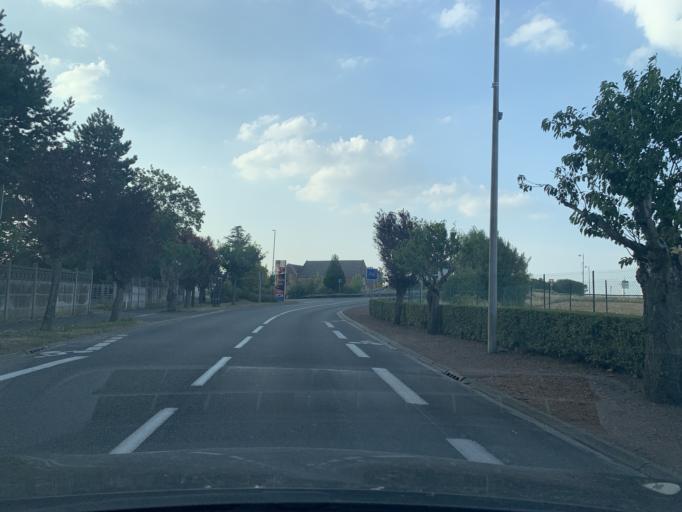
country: FR
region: Nord-Pas-de-Calais
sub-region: Departement du Nord
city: Caudry
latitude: 50.1352
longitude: 3.4006
